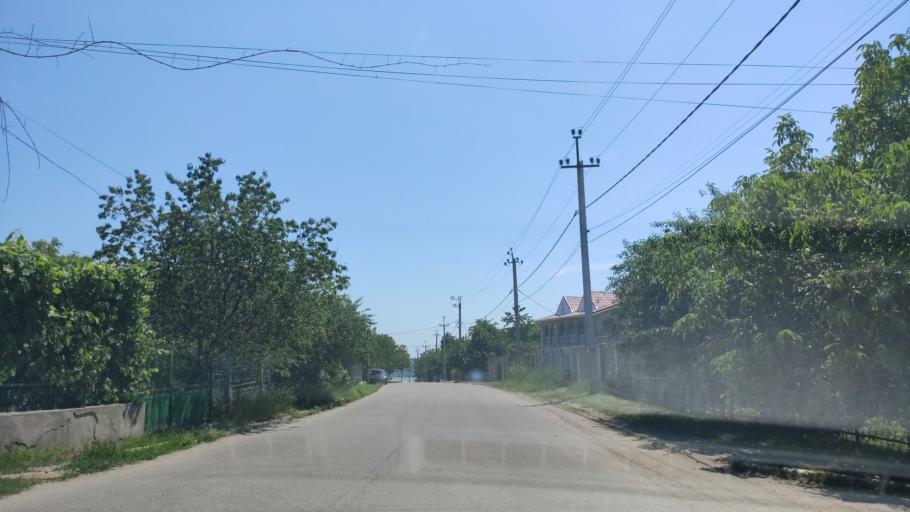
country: MD
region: Raionul Soroca
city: Soroca
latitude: 48.1499
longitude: 28.2784
